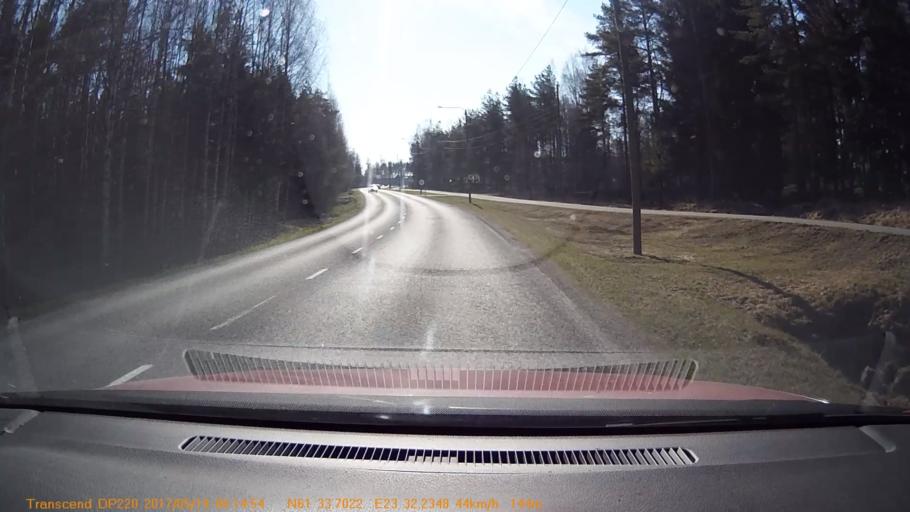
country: FI
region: Pirkanmaa
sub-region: Tampere
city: Yloejaervi
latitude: 61.5618
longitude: 23.5370
